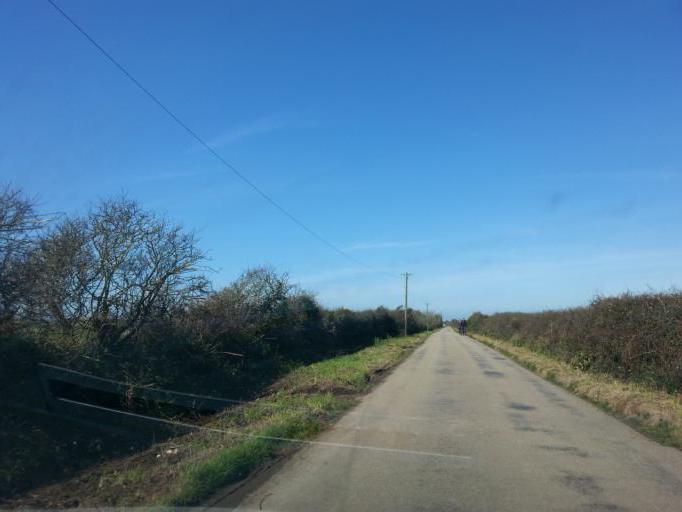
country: GB
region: England
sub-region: Cornwall
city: Landewednack
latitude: 49.9867
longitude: -5.1994
